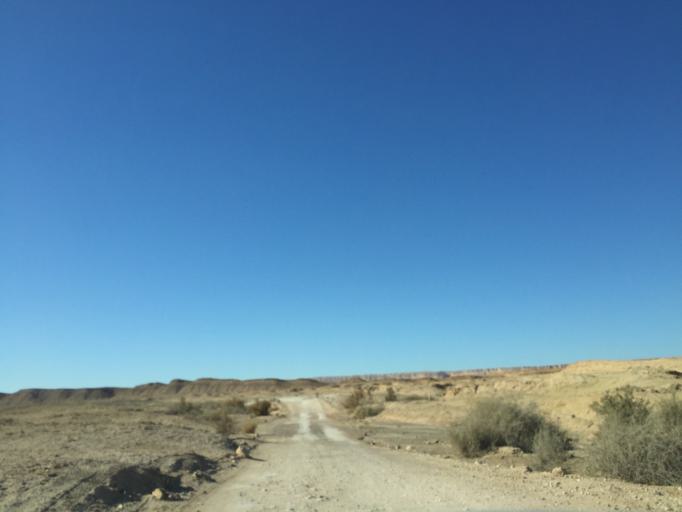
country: IL
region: Southern District
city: Mitzpe Ramon
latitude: 30.6133
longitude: 34.9093
